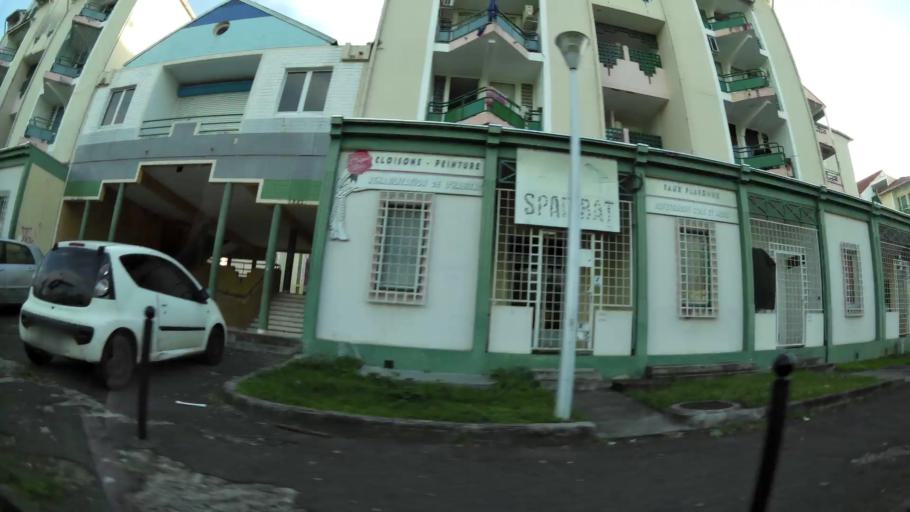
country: GP
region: Guadeloupe
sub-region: Guadeloupe
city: Pointe-a-Pitre
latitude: 16.2322
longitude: -61.5316
